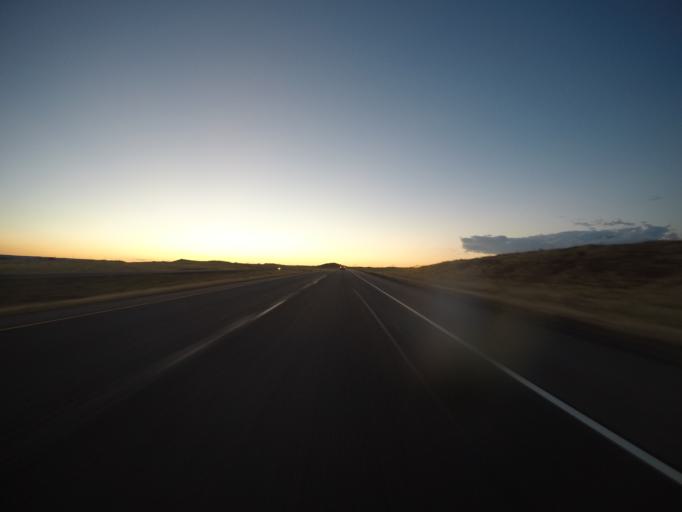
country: US
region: Wyoming
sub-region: Albany County
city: Laramie
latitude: 41.0240
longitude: -105.4252
